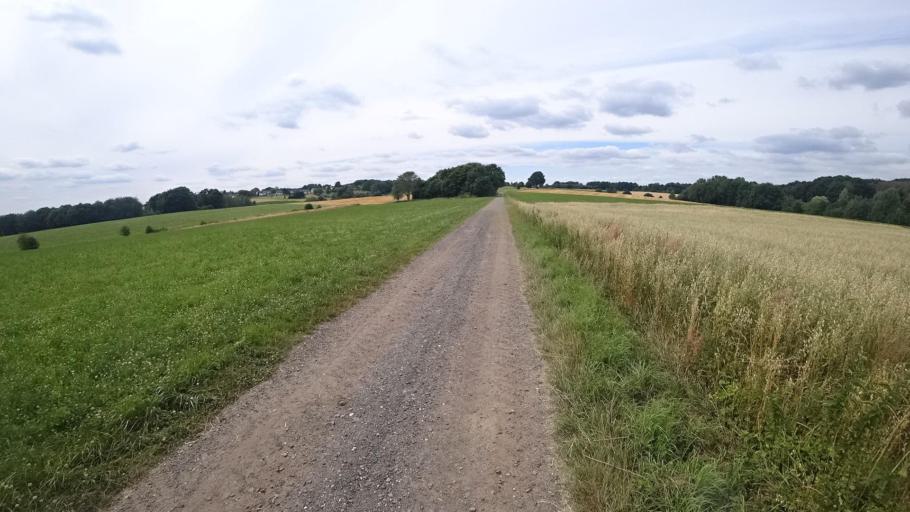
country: DE
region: Rheinland-Pfalz
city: Ziegenhain
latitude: 50.6753
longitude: 7.5378
